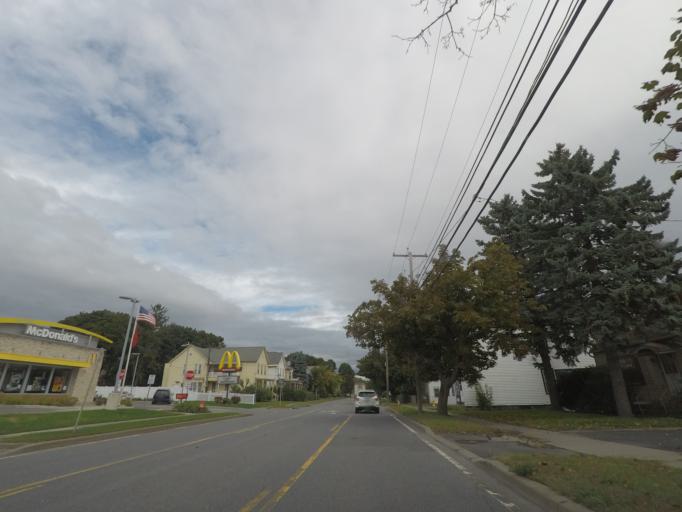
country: US
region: New York
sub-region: Albany County
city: Cohoes
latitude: 42.7823
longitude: -73.6957
